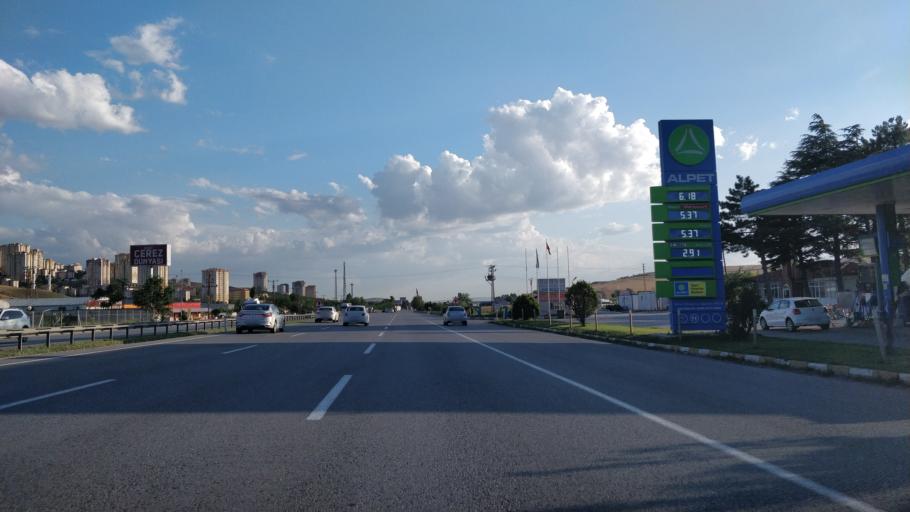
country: TR
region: Ankara
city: Etimesgut
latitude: 39.8267
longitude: 32.5760
